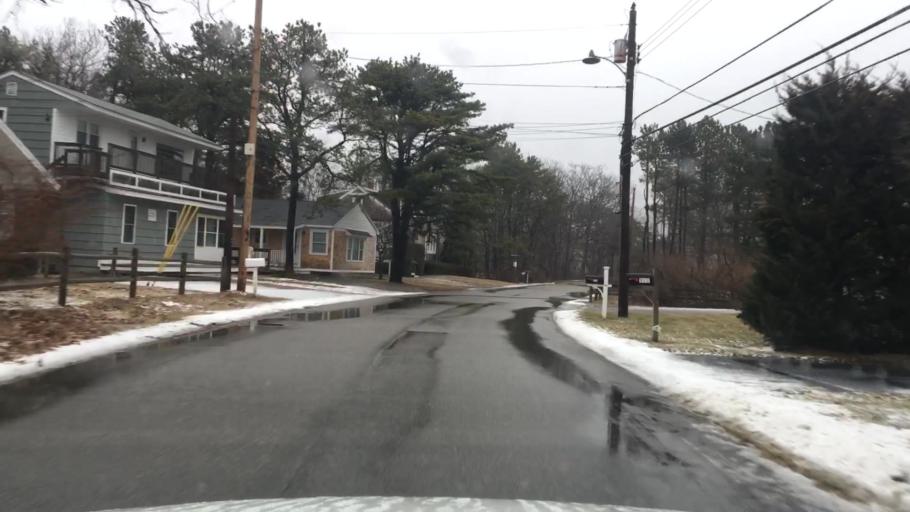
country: US
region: Maine
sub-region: York County
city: Arundel
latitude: 43.3964
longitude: -70.4217
